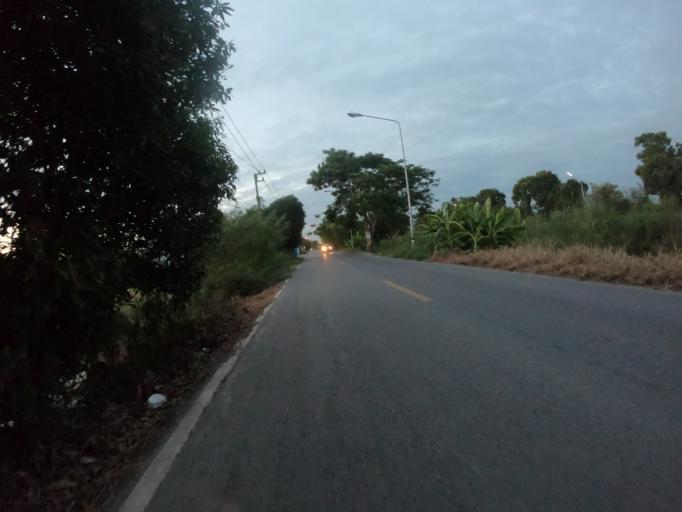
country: TH
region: Pathum Thani
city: Ban Rangsit
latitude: 14.0349
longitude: 100.8006
